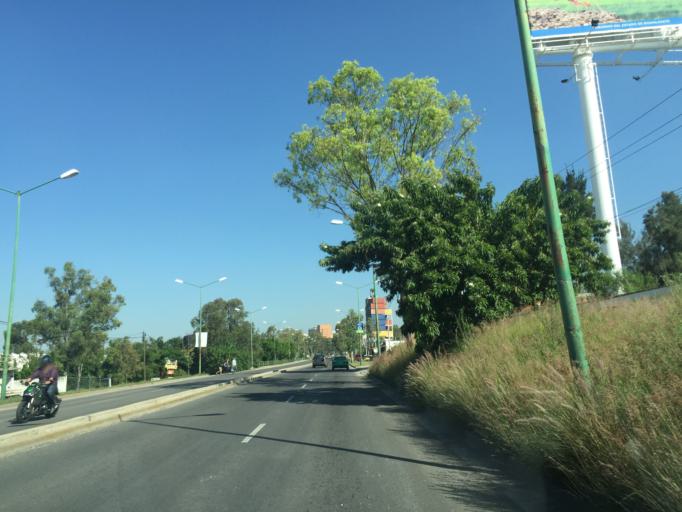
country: MX
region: Guanajuato
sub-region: Leon
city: La Ermita
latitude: 21.1634
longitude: -101.7263
